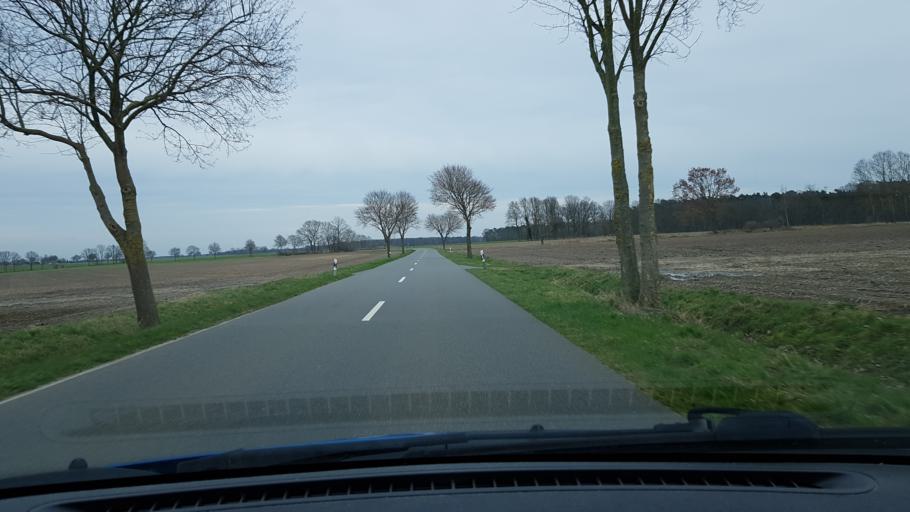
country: DE
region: Lower Saxony
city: Emmendorf
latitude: 53.0007
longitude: 10.6210
